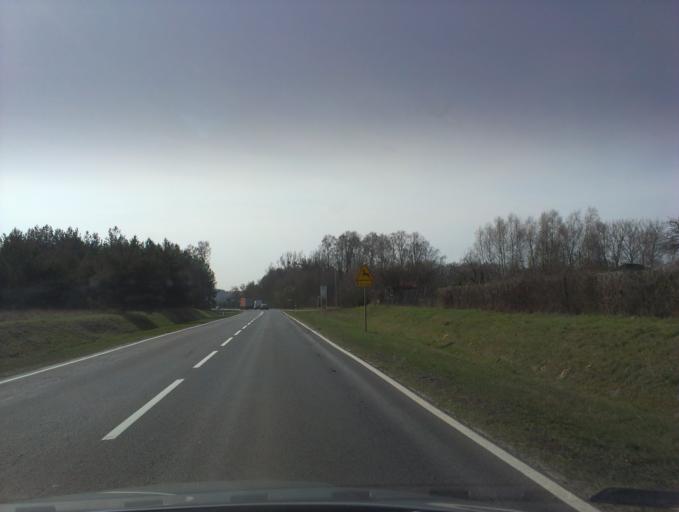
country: PL
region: Greater Poland Voivodeship
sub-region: Powiat zlotowski
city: Okonek
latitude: 53.5281
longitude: 16.8532
